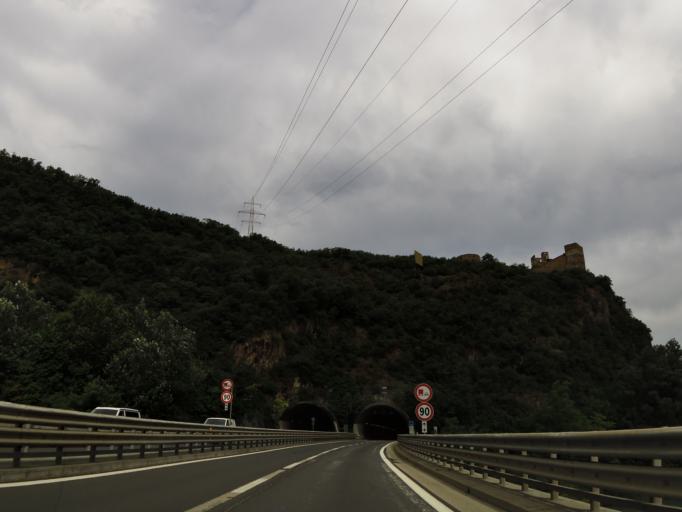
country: IT
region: Trentino-Alto Adige
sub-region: Bolzano
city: Cornaiano
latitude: 46.4779
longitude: 11.3085
